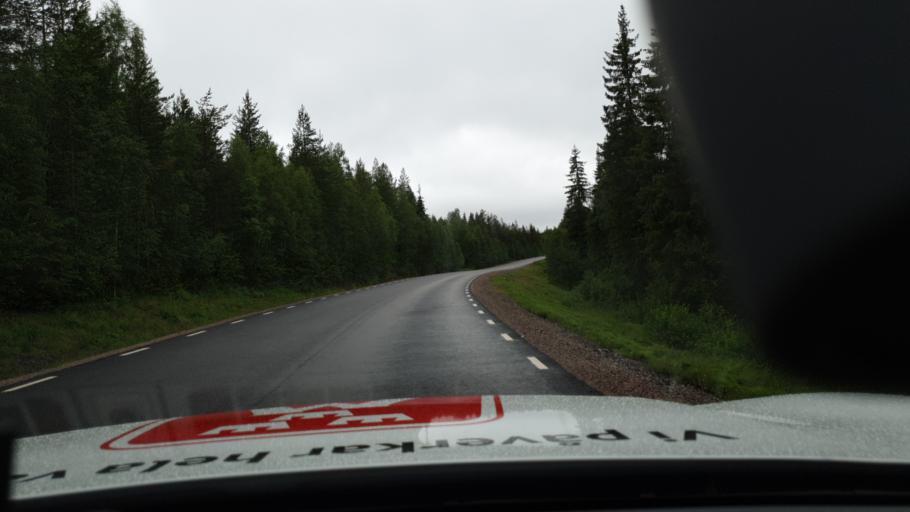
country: SE
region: Norrbotten
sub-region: Overtornea Kommun
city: OEvertornea
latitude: 66.4207
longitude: 23.5553
